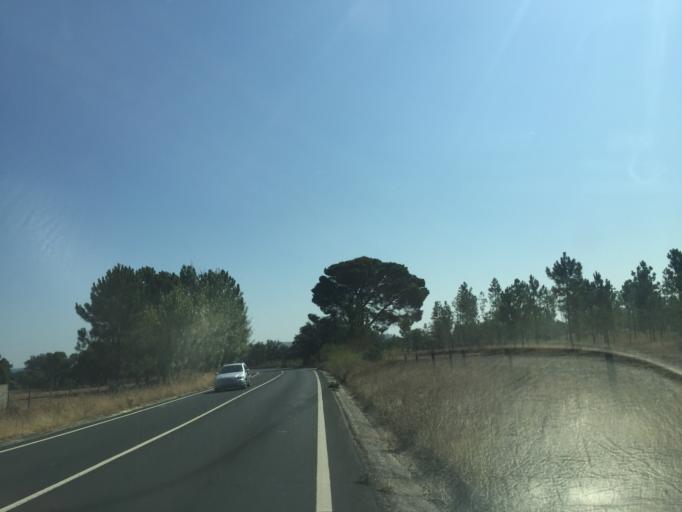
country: PT
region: Santarem
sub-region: Alpiarca
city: Alpiarca
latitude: 39.2756
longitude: -8.5490
